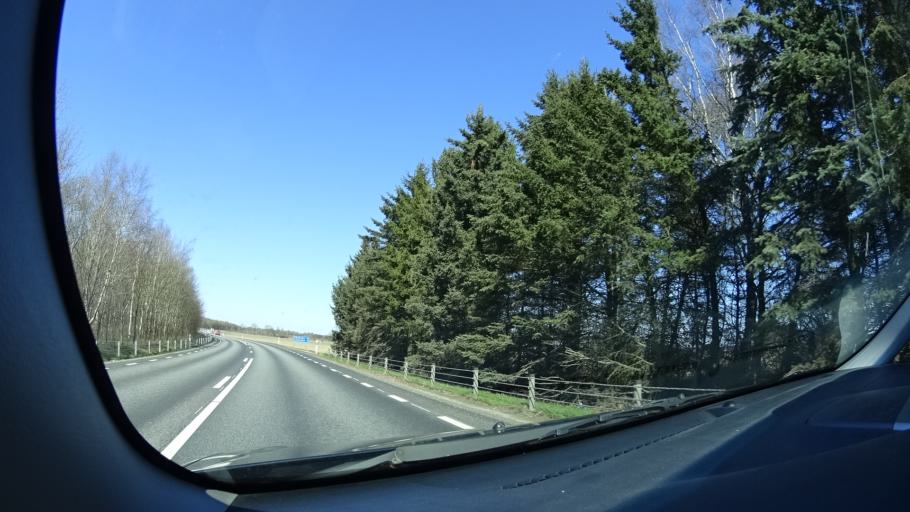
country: SE
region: Skane
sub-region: Angelholms Kommun
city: AEngelholm
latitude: 56.1953
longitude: 12.8472
